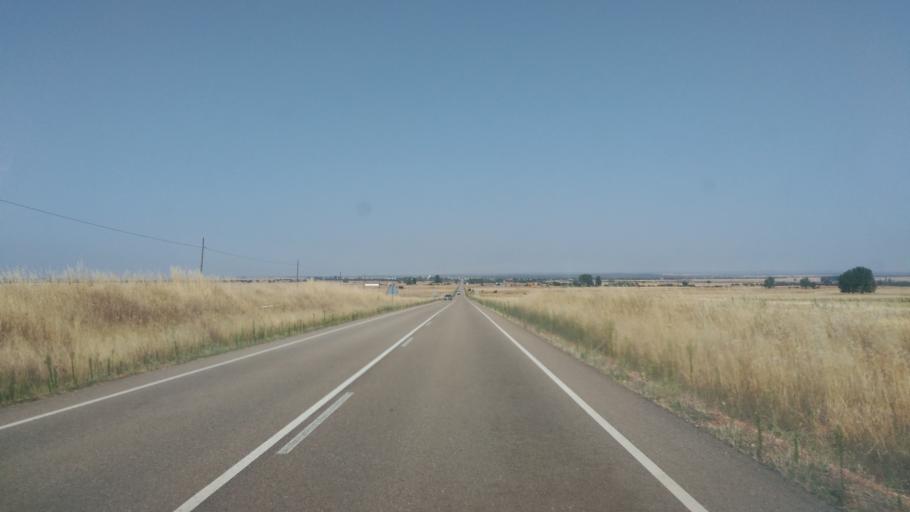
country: ES
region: Castille and Leon
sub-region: Provincia de Salamanca
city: Cabrillas
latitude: 40.7639
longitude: -6.2167
